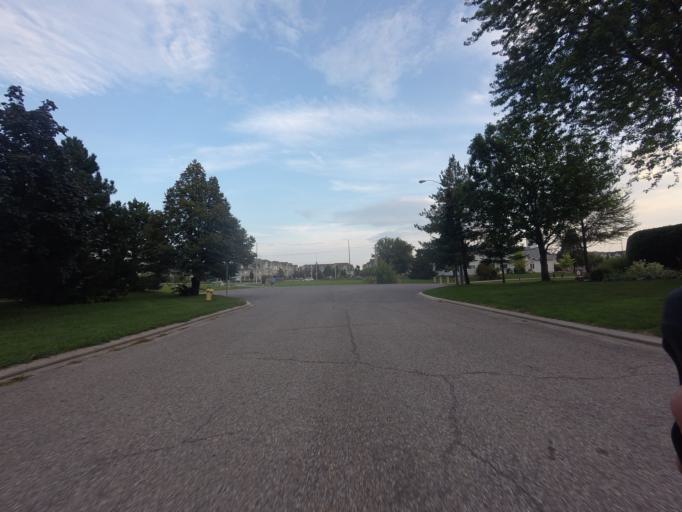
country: CA
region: Ontario
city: Bells Corners
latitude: 45.2669
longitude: -75.7565
